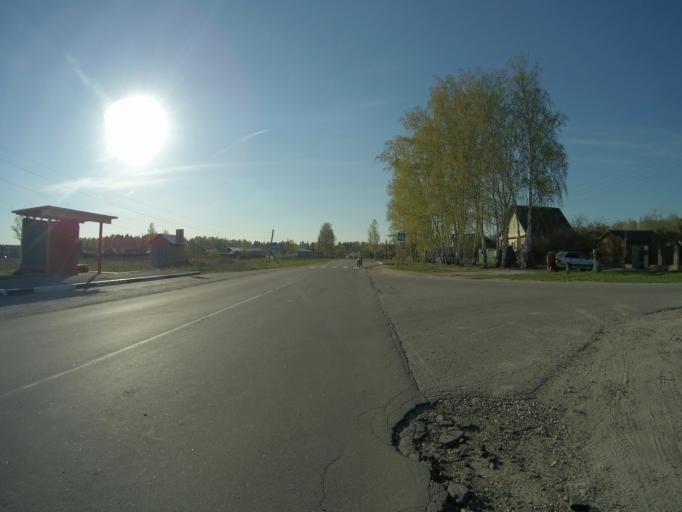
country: RU
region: Vladimir
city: Sudogda
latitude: 56.0679
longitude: 40.7997
